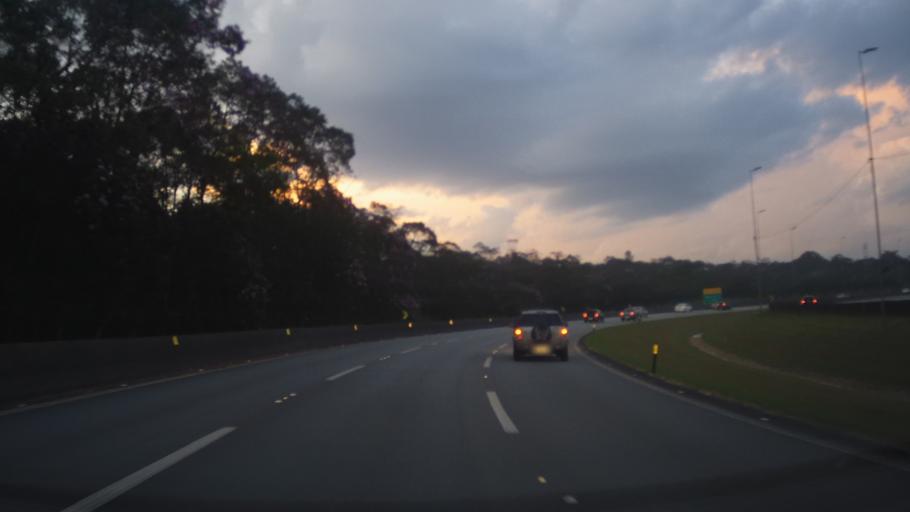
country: BR
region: Sao Paulo
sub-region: Cubatao
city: Cubatao
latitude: -23.8963
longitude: -46.5675
